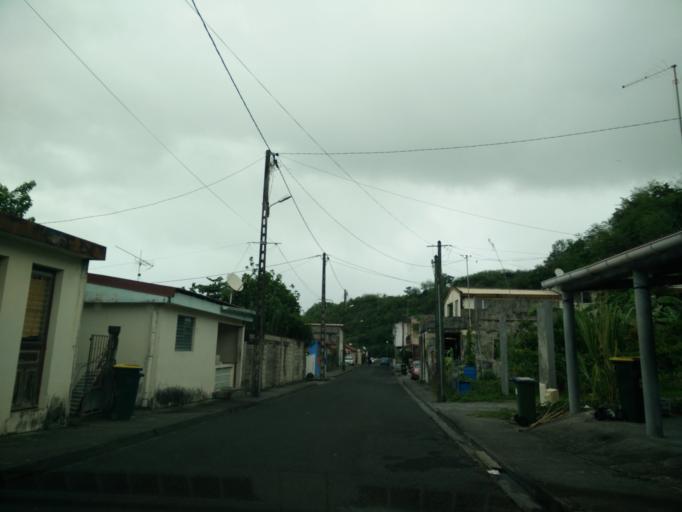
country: MQ
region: Martinique
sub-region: Martinique
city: Saint-Pierre
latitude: 14.8042
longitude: -61.2263
